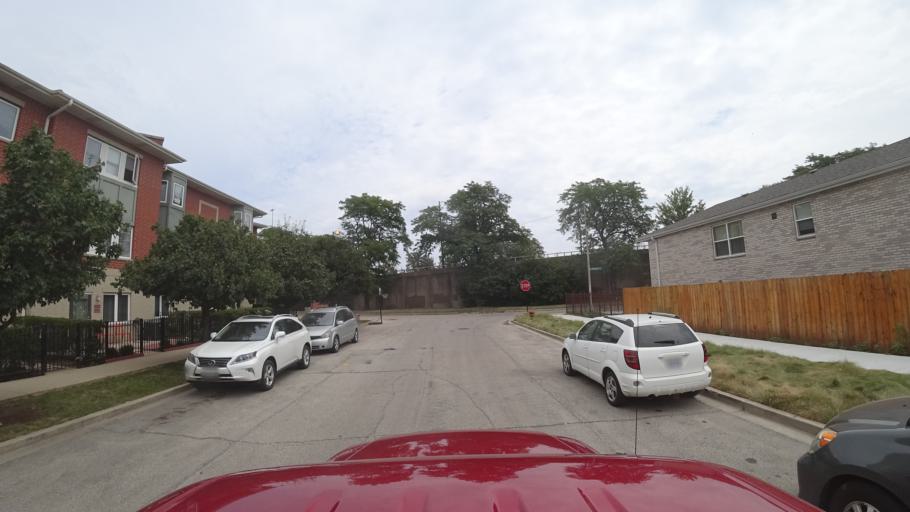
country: US
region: Illinois
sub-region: Cook County
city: Chicago
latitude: 41.8341
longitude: -87.6856
